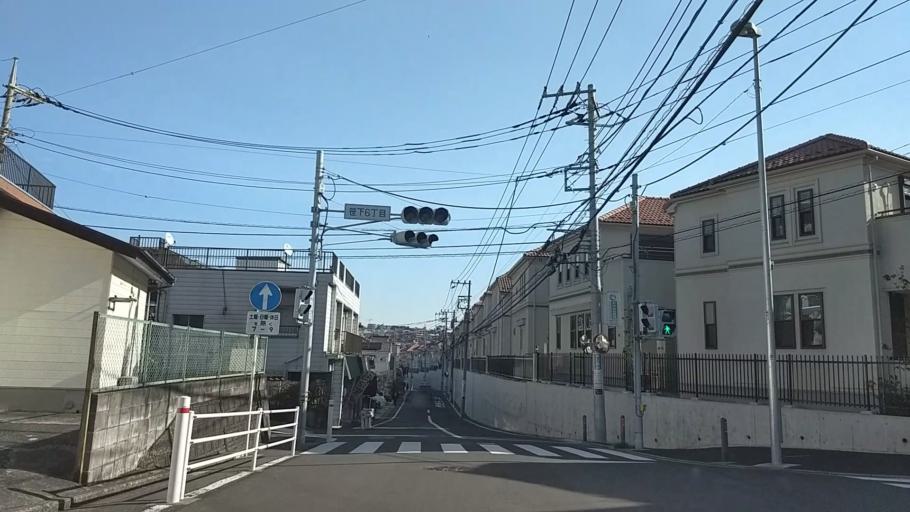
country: JP
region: Kanagawa
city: Yokohama
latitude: 35.3891
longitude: 139.5963
